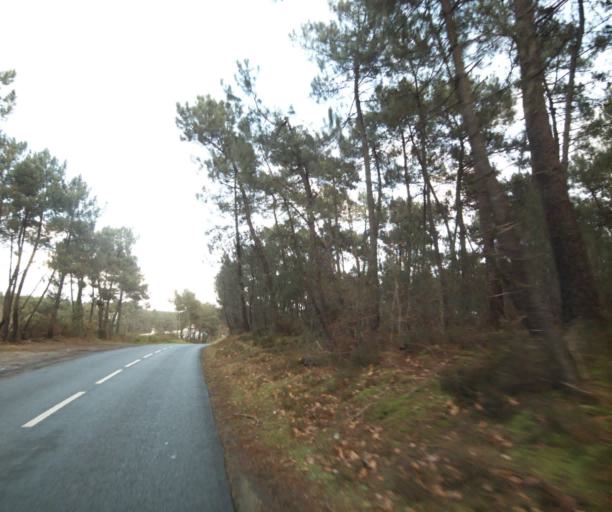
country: FR
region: Pays de la Loire
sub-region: Departement de la Sarthe
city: Ruaudin
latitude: 47.9646
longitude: 0.2288
